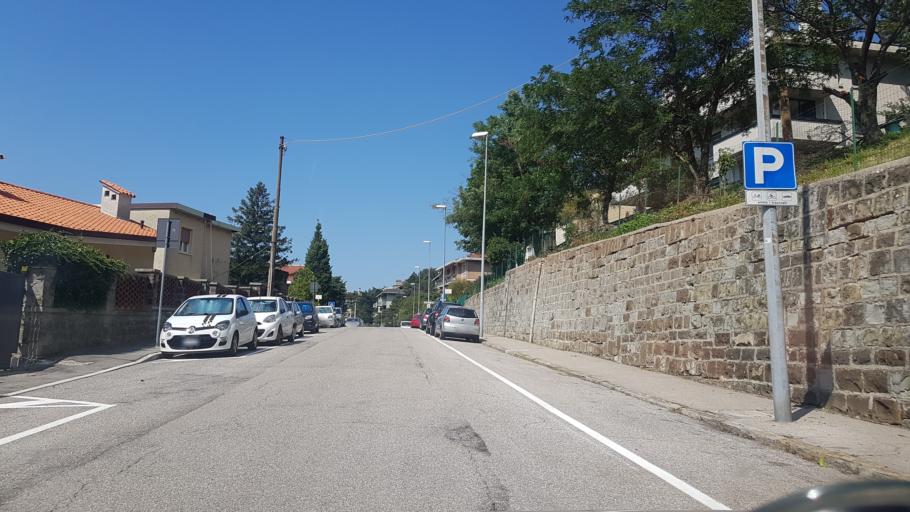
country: IT
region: Friuli Venezia Giulia
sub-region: Provincia di Trieste
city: Trieste
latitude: 45.6611
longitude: 13.7828
